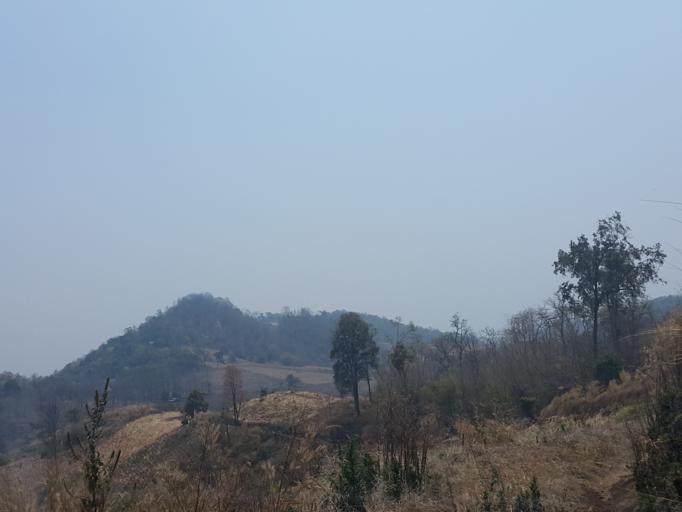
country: TH
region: Chiang Mai
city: Samoeng
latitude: 18.7832
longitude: 98.8209
